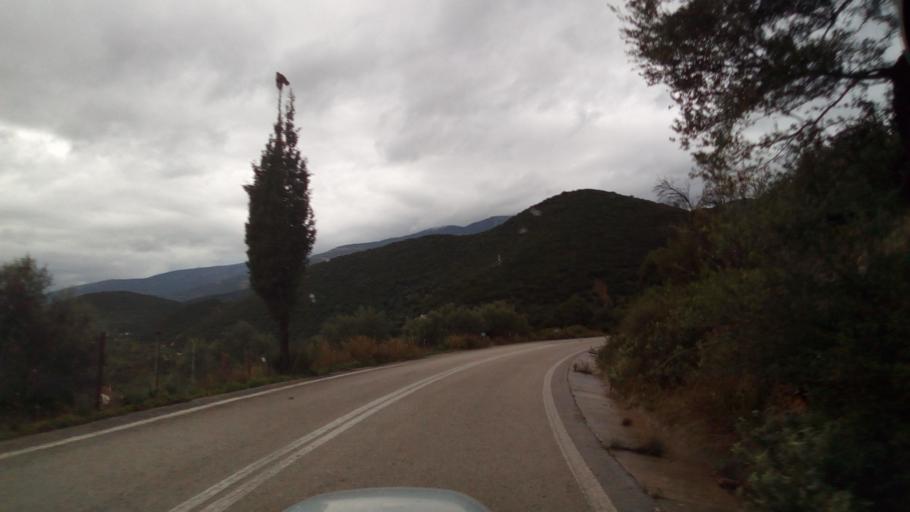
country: GR
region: West Greece
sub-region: Nomos Aitolias kai Akarnanias
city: Nafpaktos
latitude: 38.4246
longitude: 21.9357
